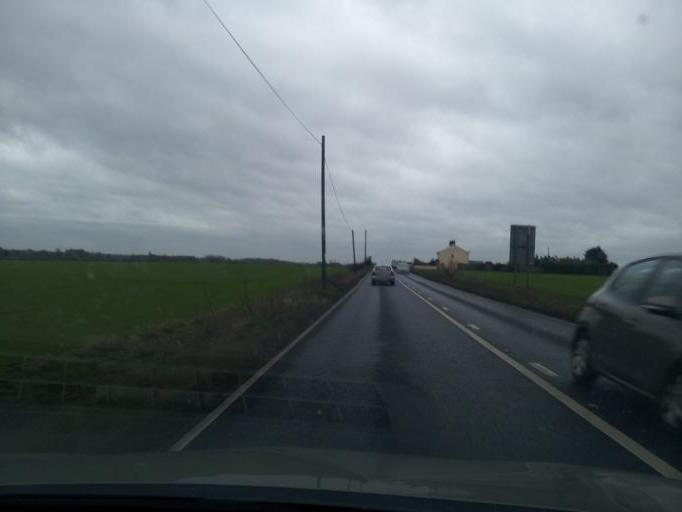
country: GB
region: England
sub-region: Suffolk
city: Thurston
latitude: 52.2810
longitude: 0.8043
